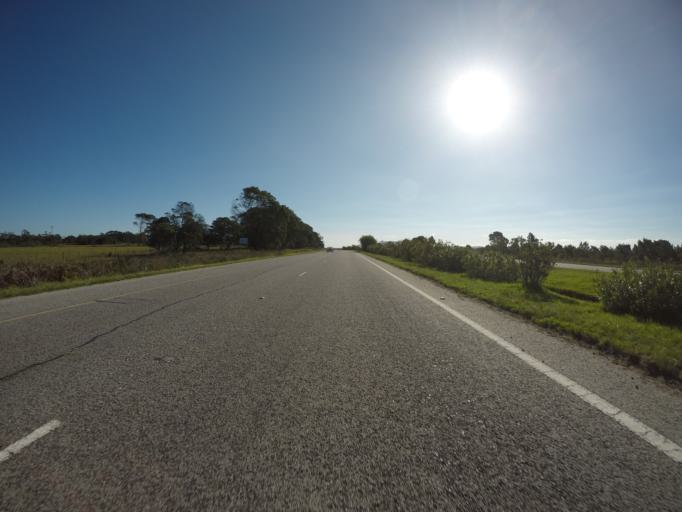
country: ZA
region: Eastern Cape
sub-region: Nelson Mandela Bay Metropolitan Municipality
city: Uitenhage
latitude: -33.9354
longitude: 25.3634
